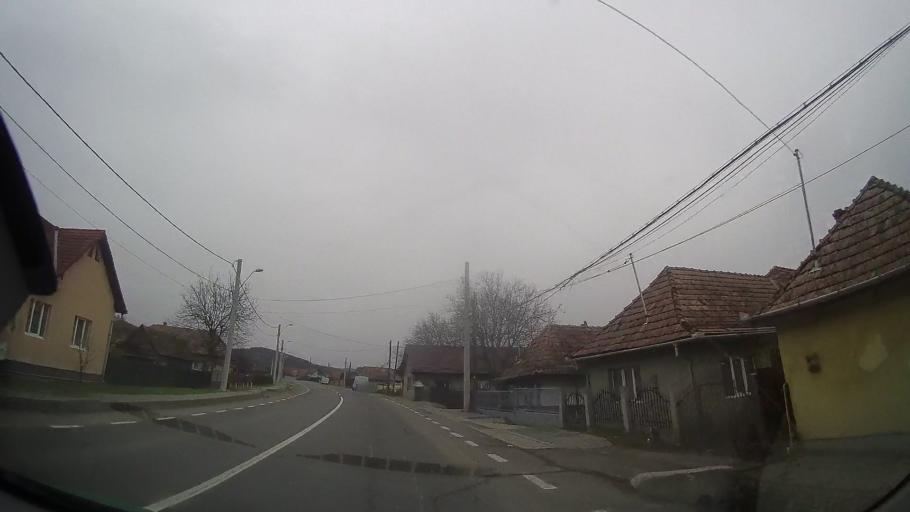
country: RO
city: Remetea
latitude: 46.6000
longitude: 24.5307
